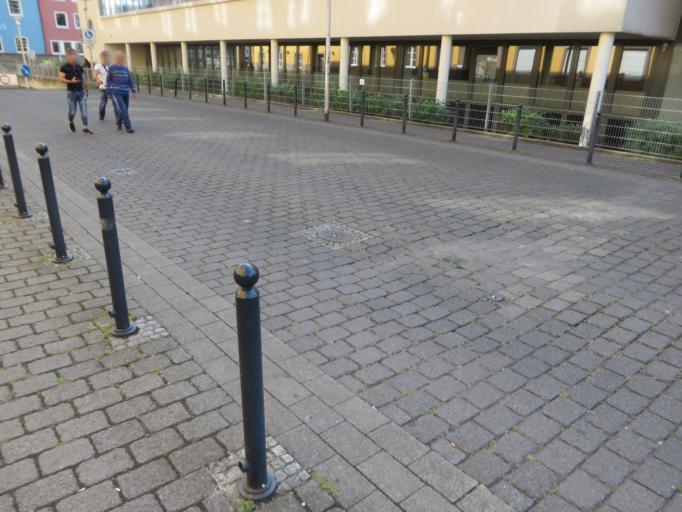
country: DE
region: North Rhine-Westphalia
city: Witten
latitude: 51.4404
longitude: 7.3345
